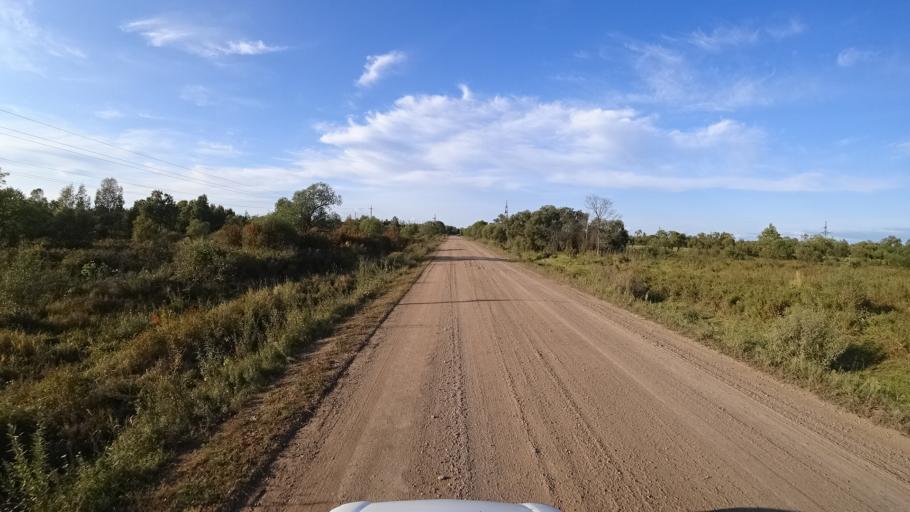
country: RU
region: Amur
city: Arkhara
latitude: 49.3634
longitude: 130.1365
